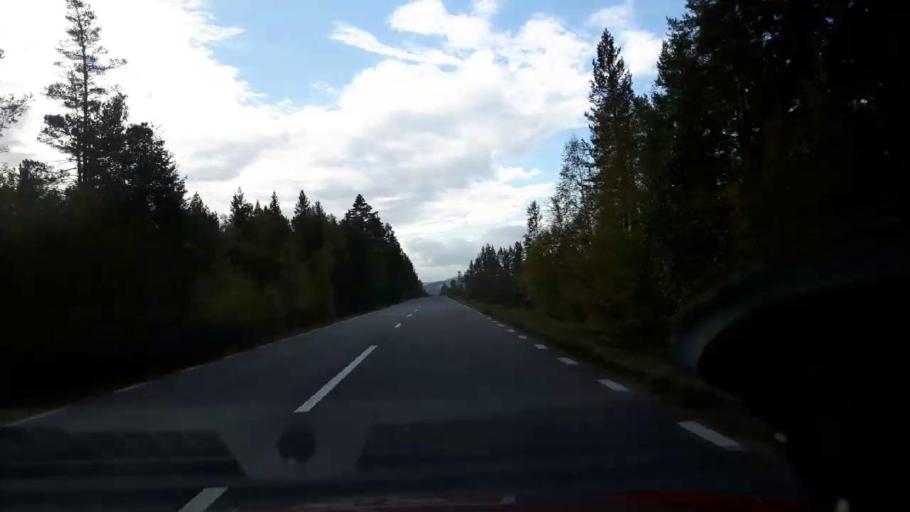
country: SE
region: Gaevleborg
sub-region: Ljusdals Kommun
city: Farila
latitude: 62.0122
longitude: 15.2407
